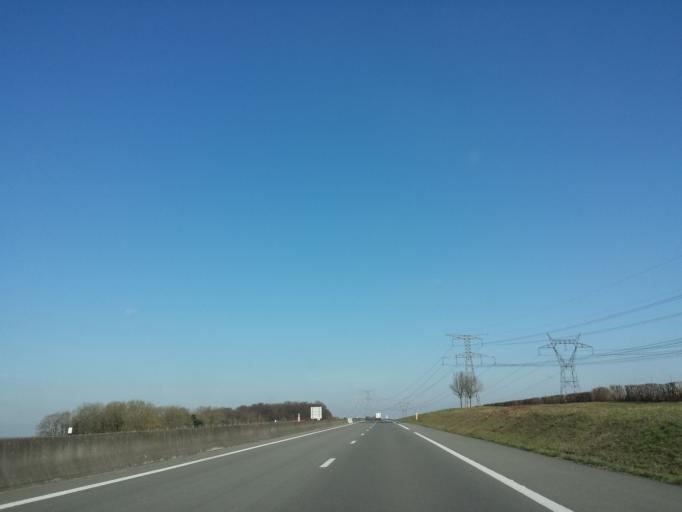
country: FR
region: Picardie
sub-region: Departement de la Somme
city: Saleux
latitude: 49.7770
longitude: 2.2359
